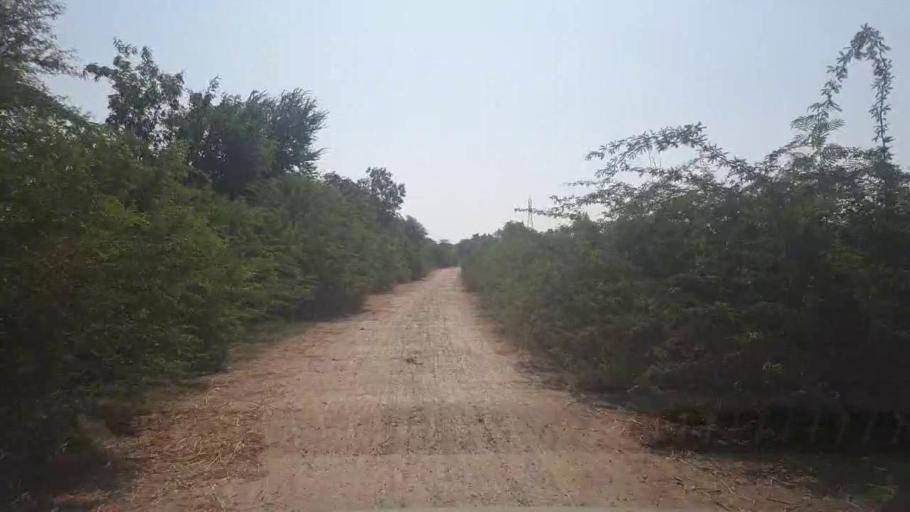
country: PK
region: Sindh
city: Badin
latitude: 24.6789
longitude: 68.8799
